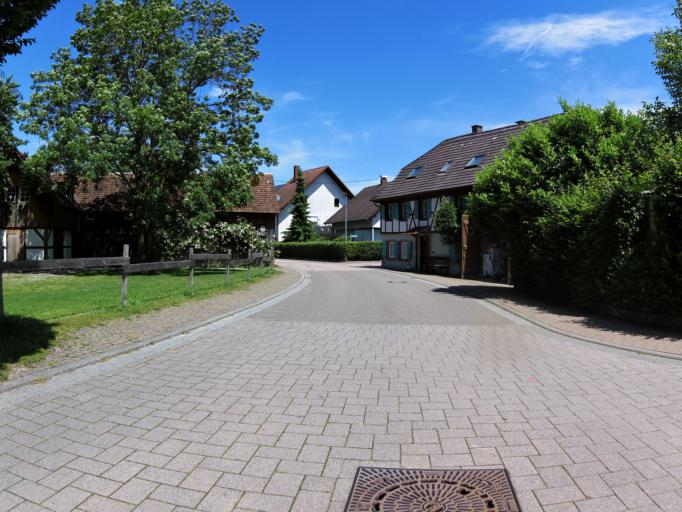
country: DE
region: Baden-Wuerttemberg
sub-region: Freiburg Region
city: Seelbach
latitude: 48.3063
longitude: 7.9398
